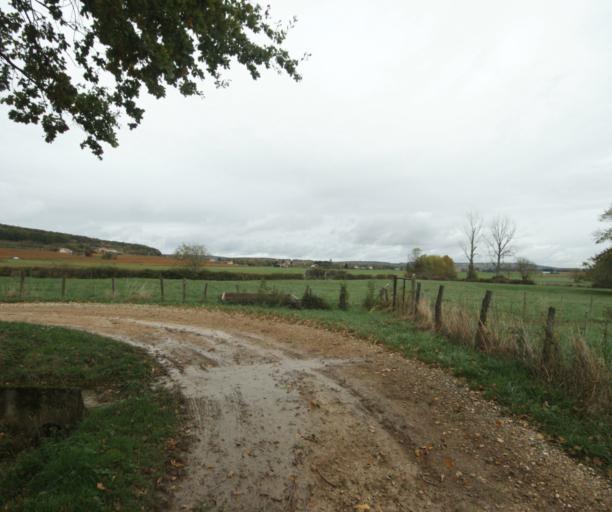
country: FR
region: Bourgogne
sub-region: Departement de Saone-et-Loire
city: Saint-Martin-Belle-Roche
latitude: 46.4619
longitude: 4.8526
